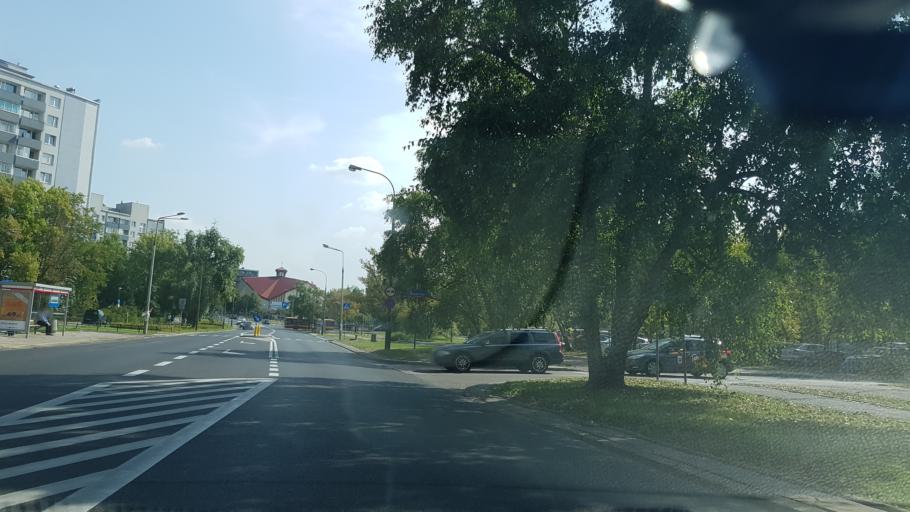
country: PL
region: Masovian Voivodeship
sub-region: Warszawa
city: Bielany
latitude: 52.2739
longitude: 20.9241
